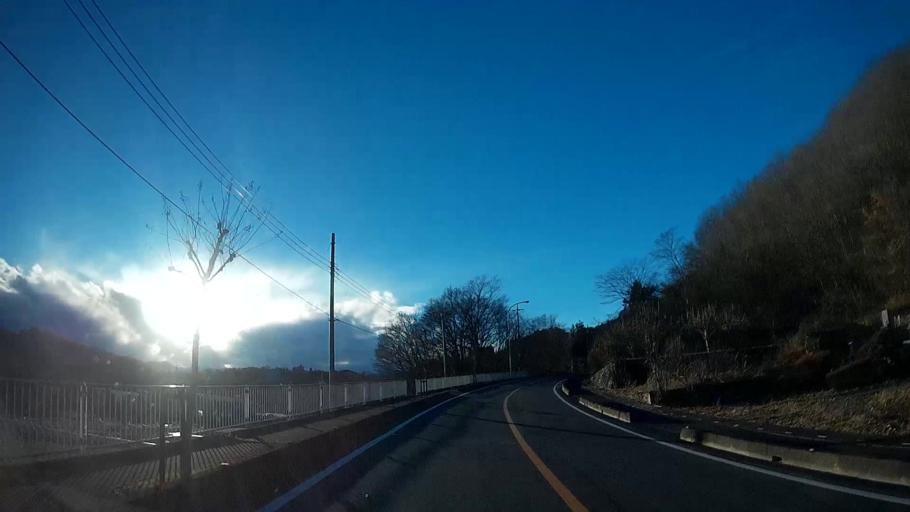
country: JP
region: Saitama
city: Chichibu
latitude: 36.0432
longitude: 139.0174
